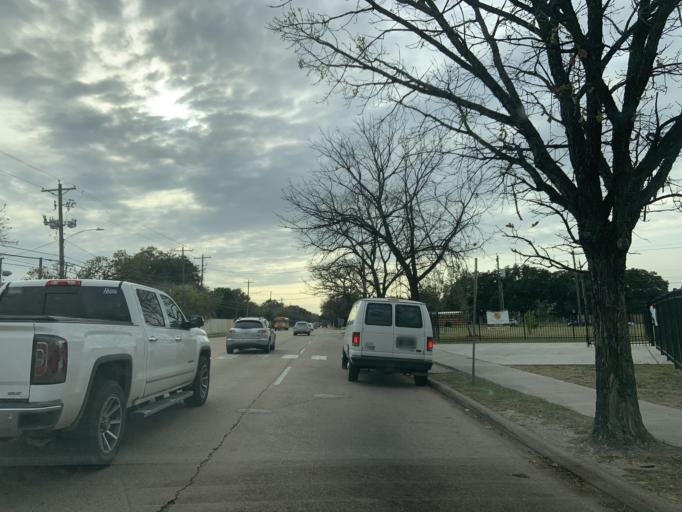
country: US
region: Texas
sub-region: Harris County
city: Bellaire
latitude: 29.6829
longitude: -95.5166
